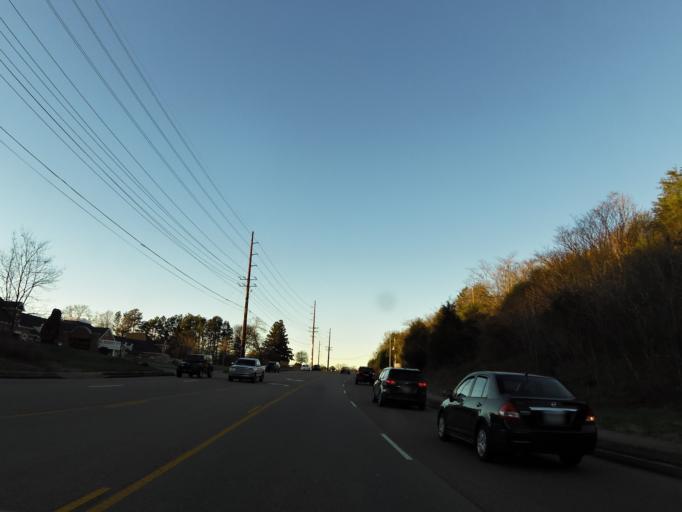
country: US
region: Tennessee
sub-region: Blount County
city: Louisville
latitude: 35.8964
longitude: -84.0709
